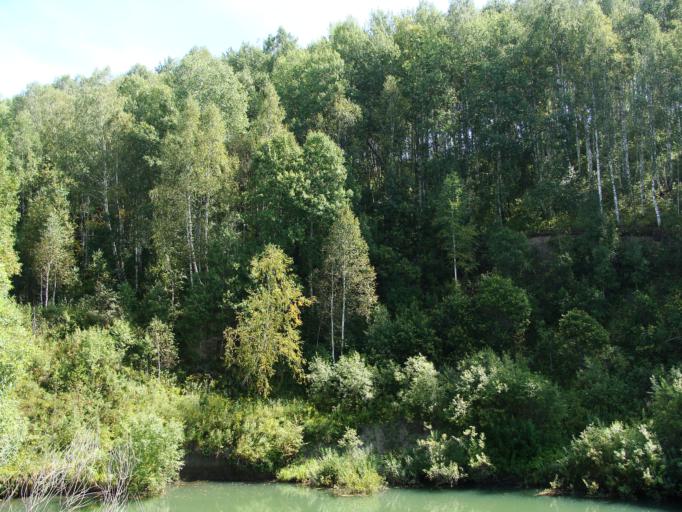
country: RU
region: Altai Krai
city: Troitskoye
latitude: 53.0826
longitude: 84.9853
